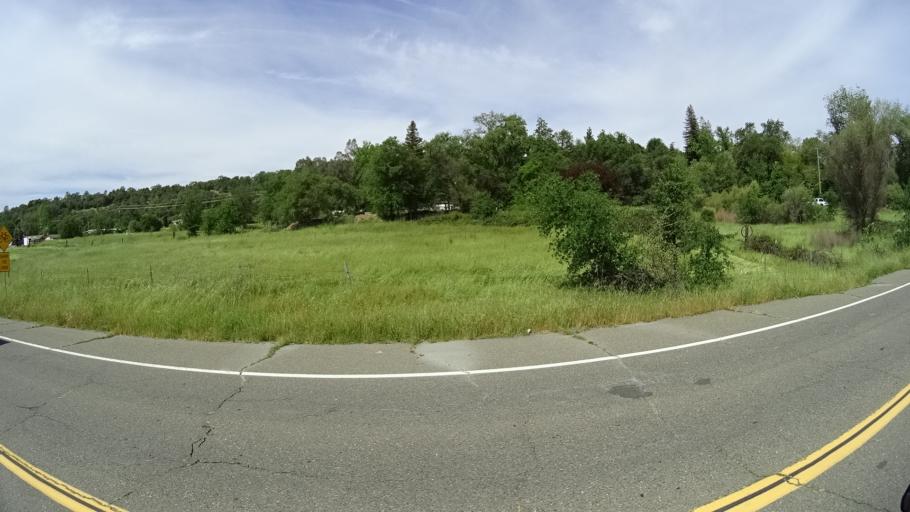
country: US
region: California
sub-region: Placer County
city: Loomis
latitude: 38.8310
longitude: -121.2175
